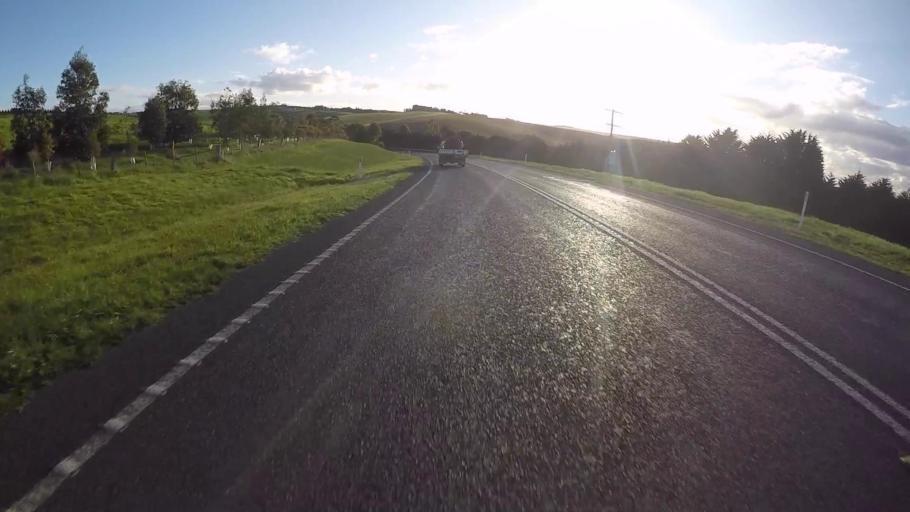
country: AU
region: Victoria
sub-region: Greater Geelong
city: Wandana Heights
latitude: -38.1692
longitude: 144.2438
